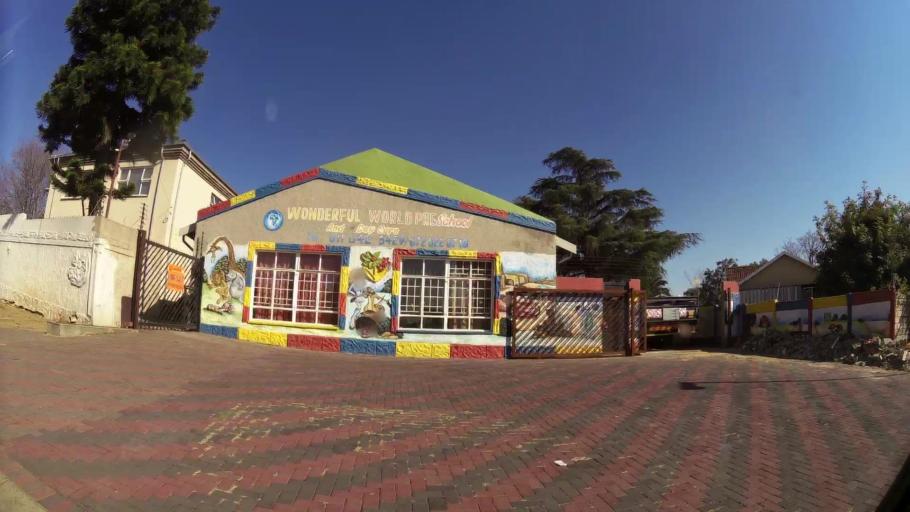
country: ZA
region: Gauteng
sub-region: Ekurhuleni Metropolitan Municipality
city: Germiston
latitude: -26.2431
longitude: 28.1097
